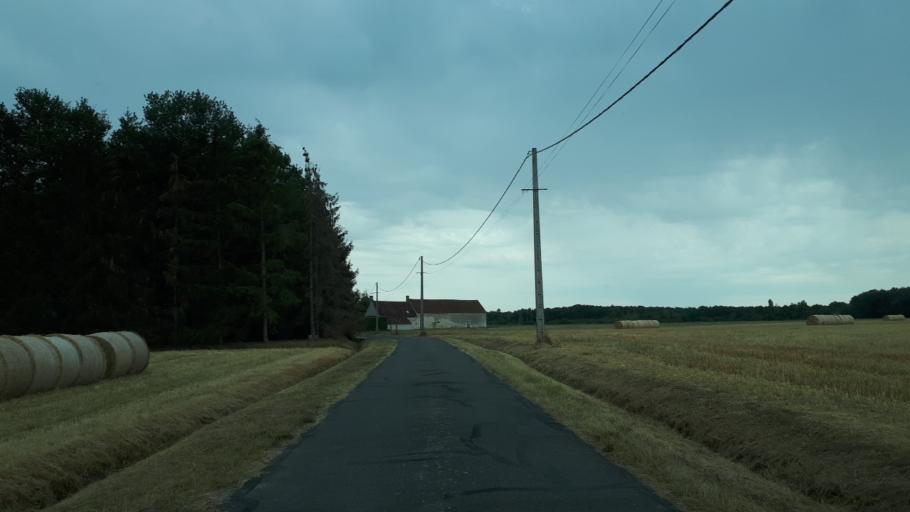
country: FR
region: Centre
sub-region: Departement du Loir-et-Cher
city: Saint-Romain-sur-Cher
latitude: 47.3562
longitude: 1.3932
